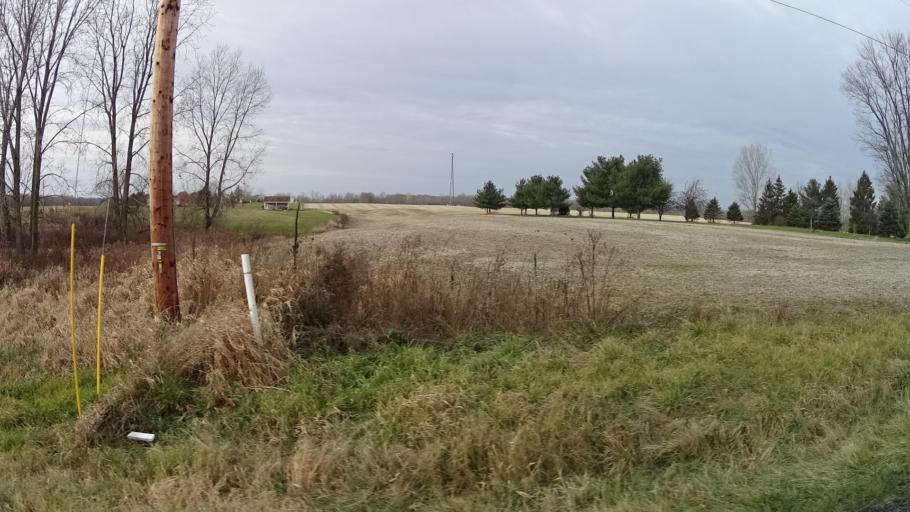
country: US
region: Ohio
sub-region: Lorain County
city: Lagrange
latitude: 41.1552
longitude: -82.1225
